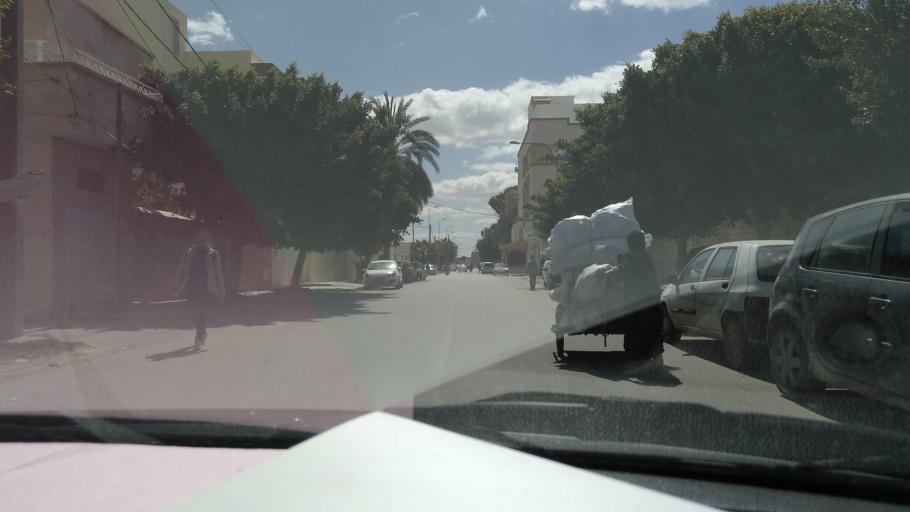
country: TN
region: Al Qayrawan
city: Kairouan
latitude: 35.6684
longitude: 10.1077
